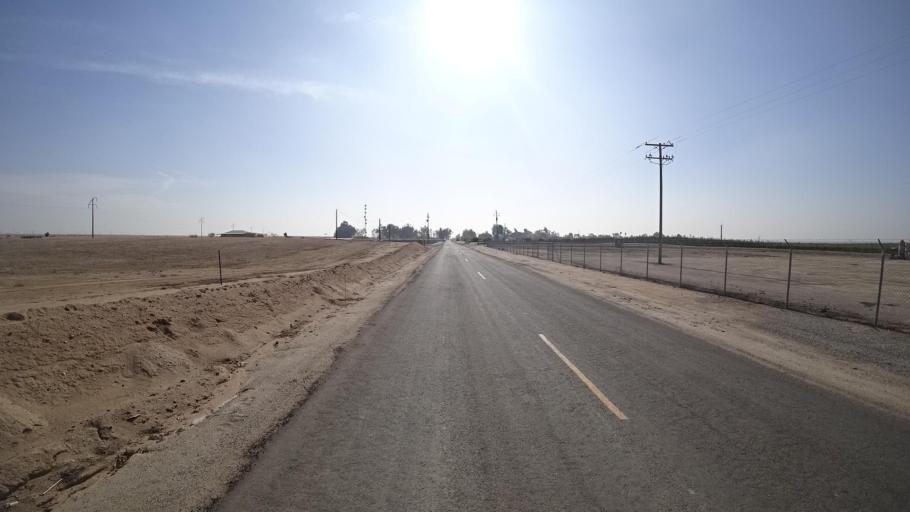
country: US
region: California
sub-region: Kern County
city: Oildale
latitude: 35.5279
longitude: -119.1083
